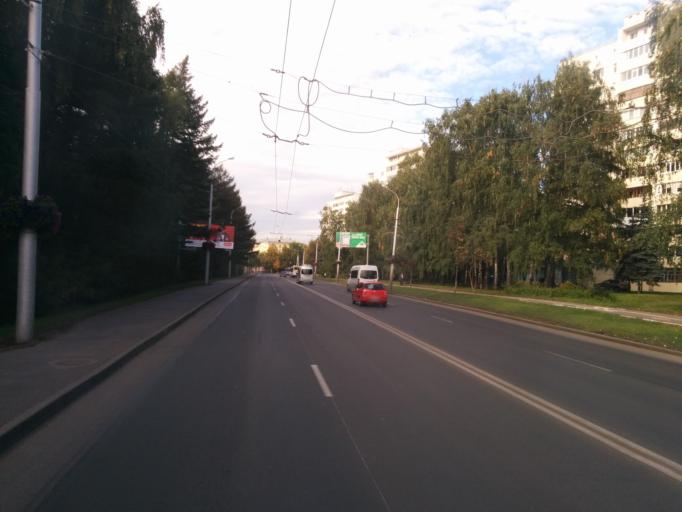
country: RU
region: Bashkortostan
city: Ufa
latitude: 54.8139
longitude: 56.0570
